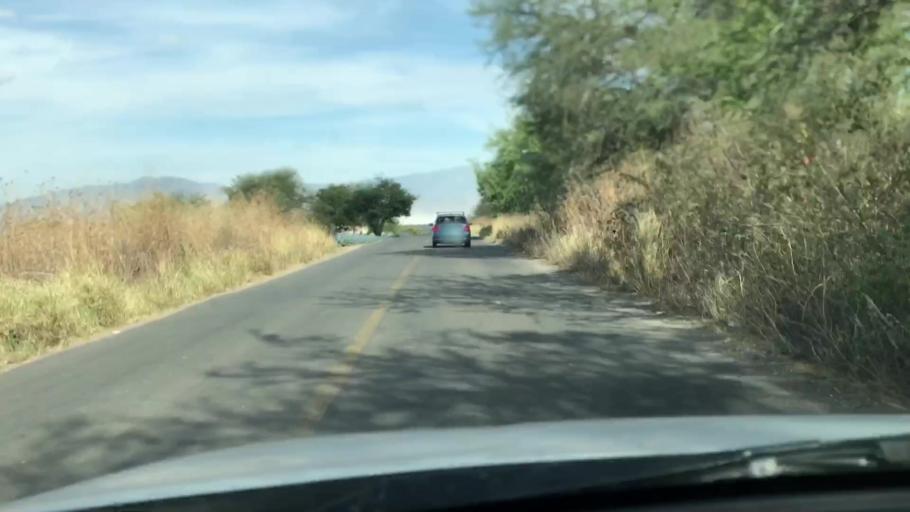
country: MX
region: Jalisco
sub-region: Zacoalco de Torres
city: Barranca de Otates (Barranca de Otatan)
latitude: 20.2740
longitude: -103.6330
